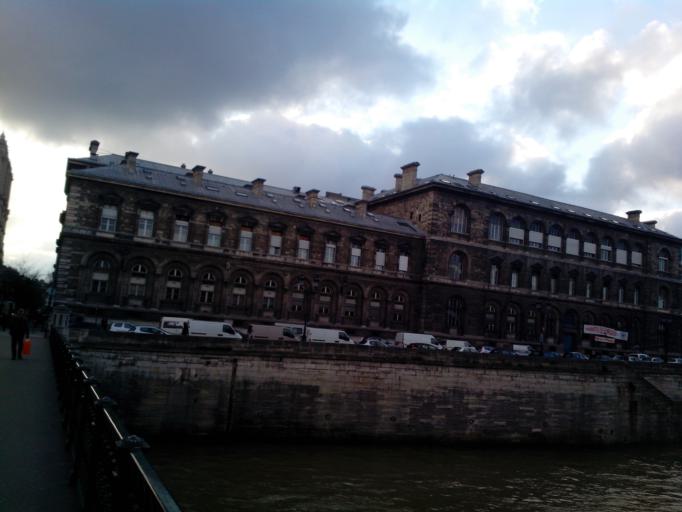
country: FR
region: Ile-de-France
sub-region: Paris
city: Paris
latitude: 48.8555
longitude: 2.3505
